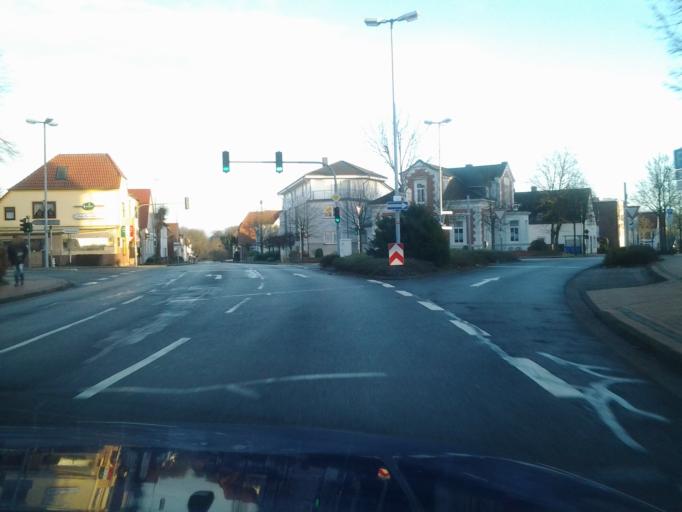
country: DE
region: Lower Saxony
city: Osterholz-Scharmbeck
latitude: 53.2263
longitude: 8.7939
